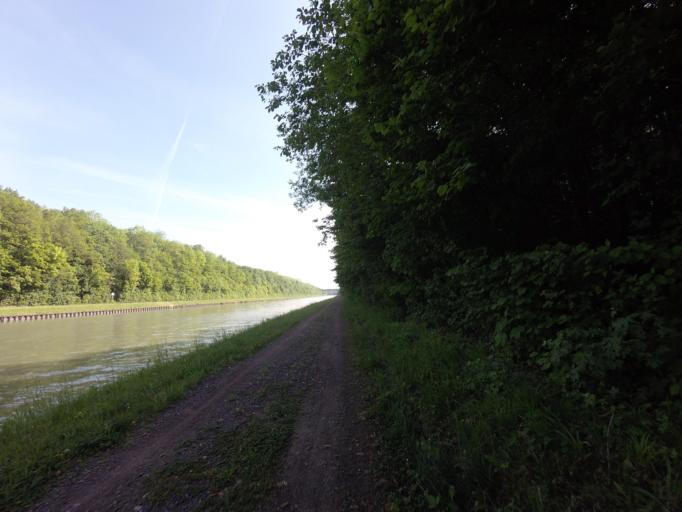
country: DE
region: Lower Saxony
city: Vordorf
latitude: 52.3415
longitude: 10.5292
